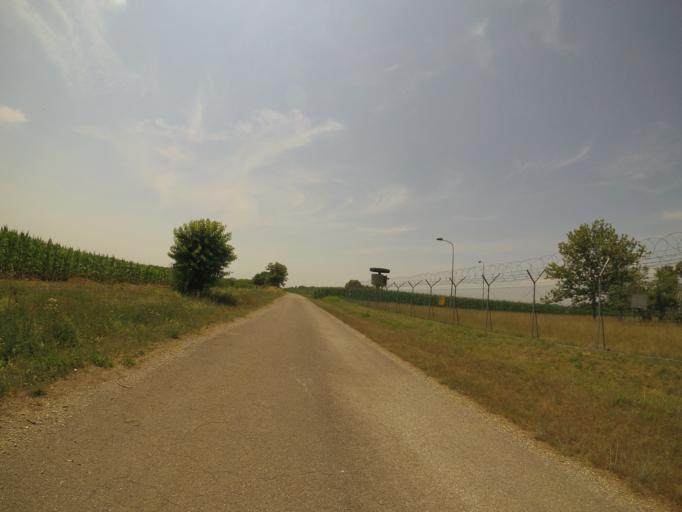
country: IT
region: Friuli Venezia Giulia
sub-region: Provincia di Udine
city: Bertiolo
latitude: 45.9546
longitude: 13.0405
